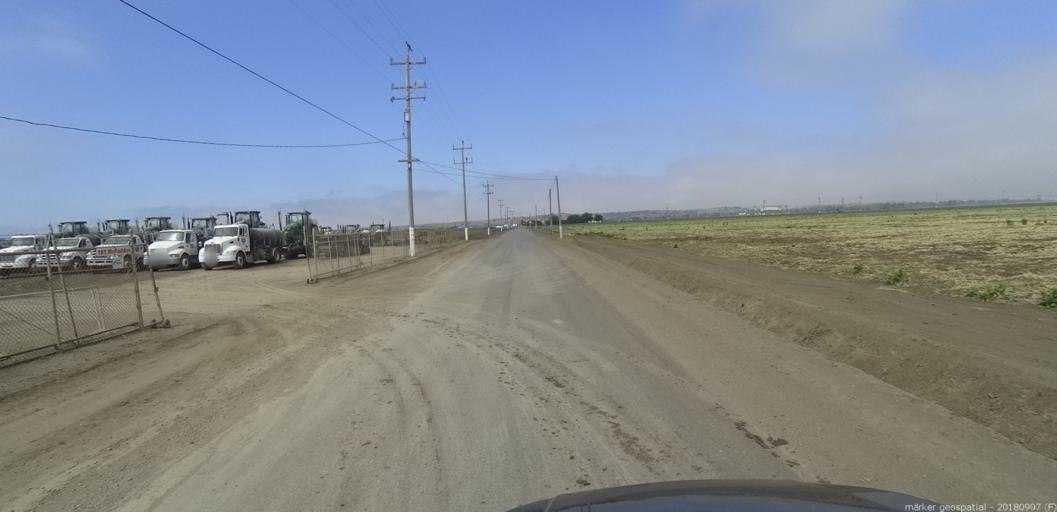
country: US
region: California
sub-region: Monterey County
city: Boronda
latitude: 36.6932
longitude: -121.7307
